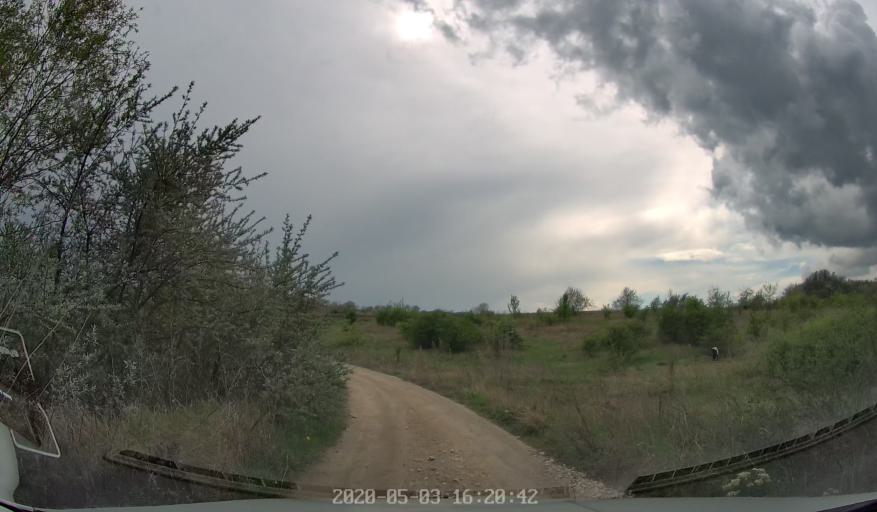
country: MD
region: Calarasi
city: Calarasi
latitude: 47.2025
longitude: 28.3490
